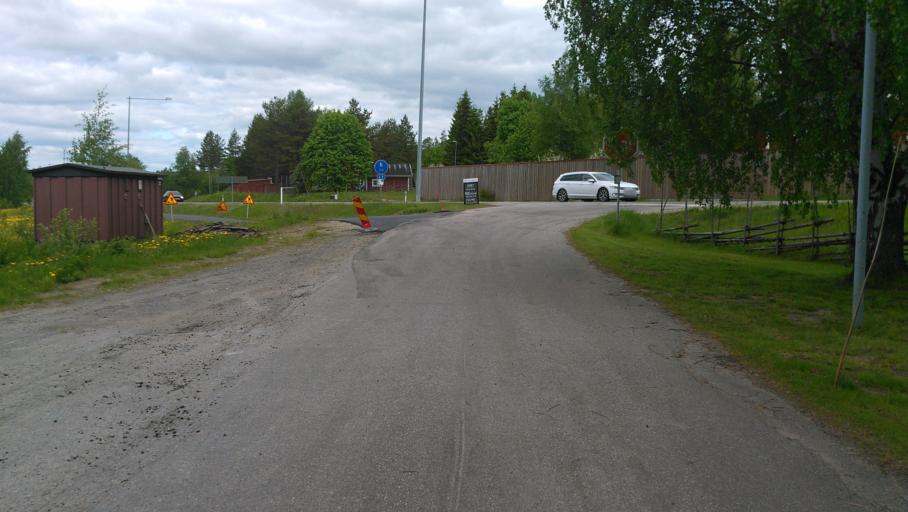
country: SE
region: Vaesterbotten
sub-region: Umea Kommun
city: Roback
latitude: 63.8604
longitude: 20.0892
